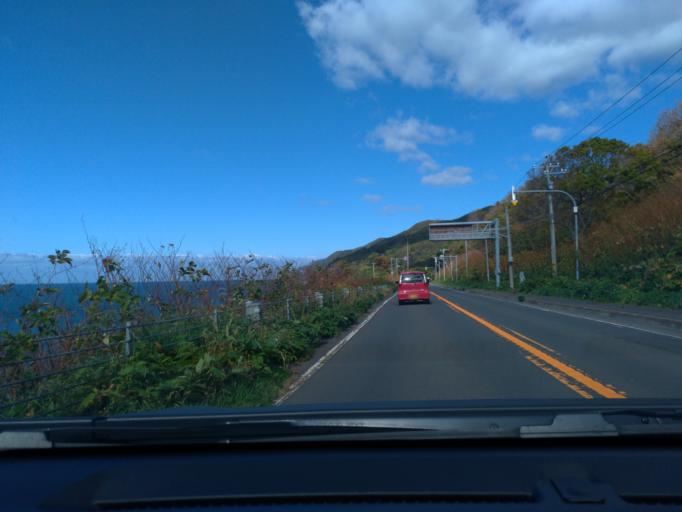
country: JP
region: Hokkaido
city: Ishikari
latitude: 43.4162
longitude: 141.4301
